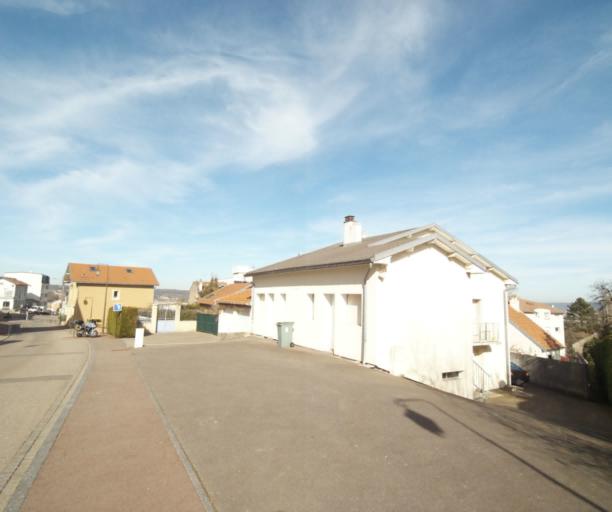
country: FR
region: Lorraine
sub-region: Departement de Meurthe-et-Moselle
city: Villers-les-Nancy
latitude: 48.6601
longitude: 6.1649
